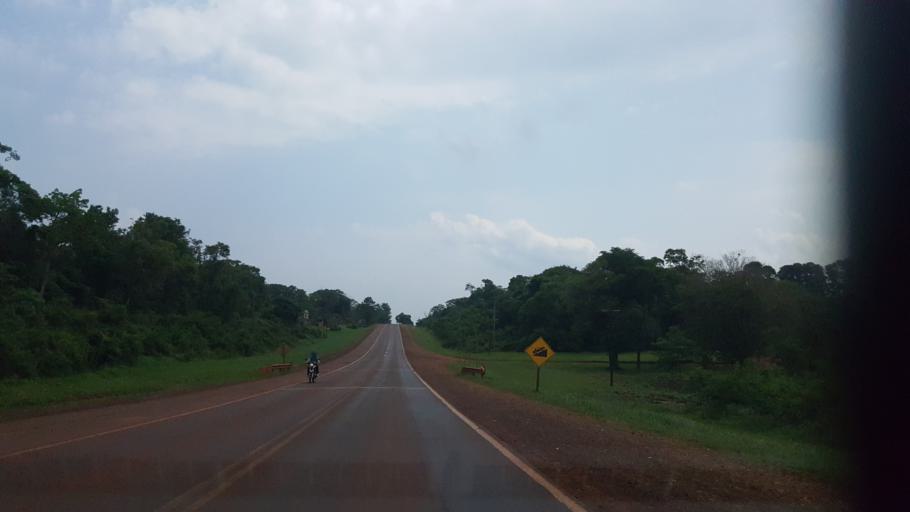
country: AR
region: Misiones
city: Jardin America
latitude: -27.0517
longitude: -55.2495
